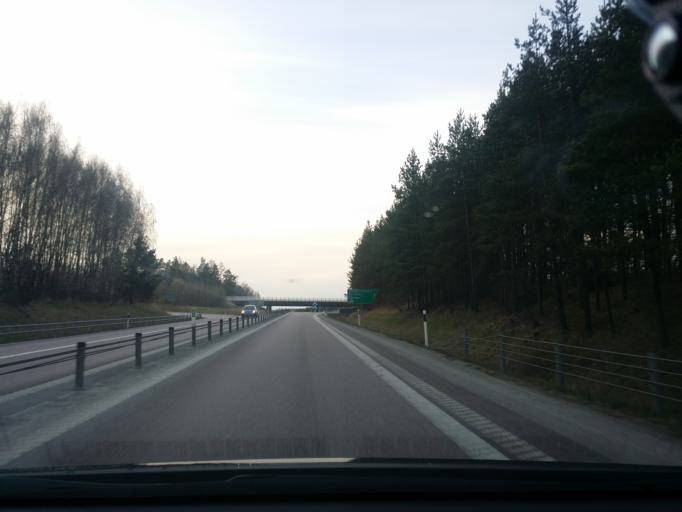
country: SE
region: Uppsala
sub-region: Enkopings Kommun
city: Enkoping
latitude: 59.6423
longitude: 17.0539
